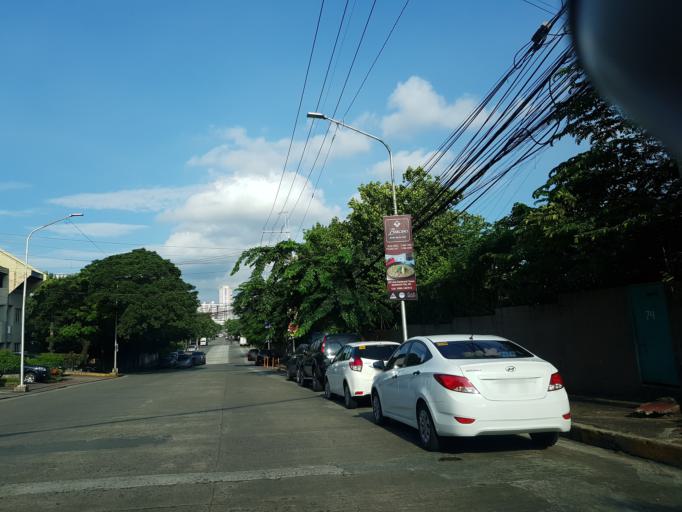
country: PH
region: Metro Manila
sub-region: Pasig
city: Pasig City
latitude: 14.6011
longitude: 121.0734
